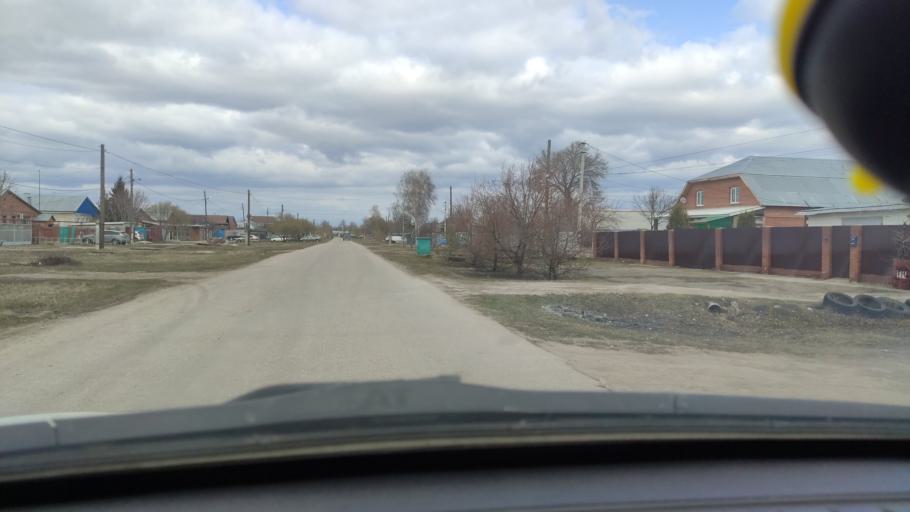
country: RU
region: Samara
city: Tol'yatti
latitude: 53.5638
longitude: 49.3999
